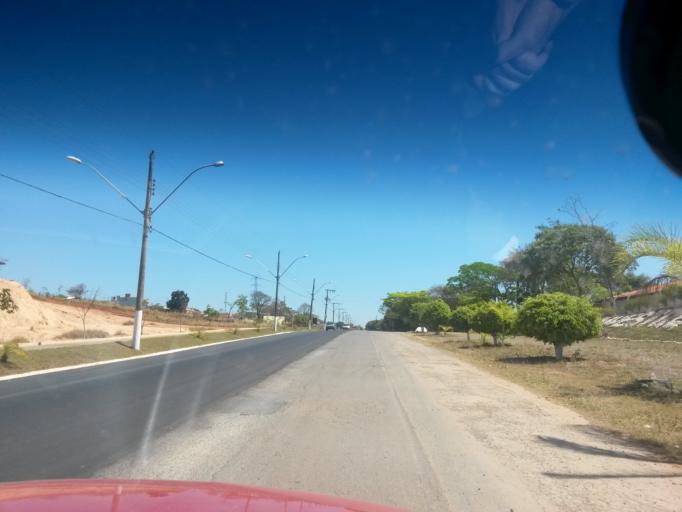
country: BR
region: Minas Gerais
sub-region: Bambui
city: Bambui
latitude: -20.0150
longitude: -45.9585
